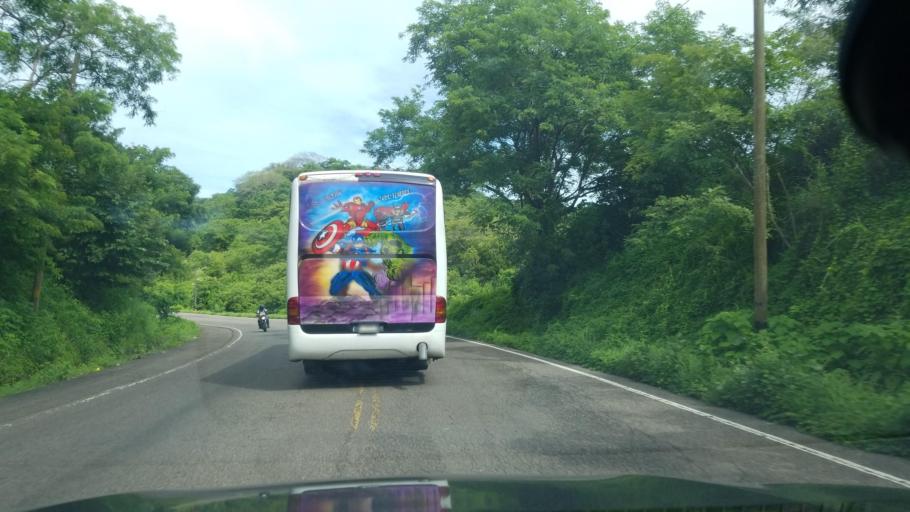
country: HN
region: Choluteca
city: Santa Ana de Yusguare
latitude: 13.3737
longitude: -87.0717
